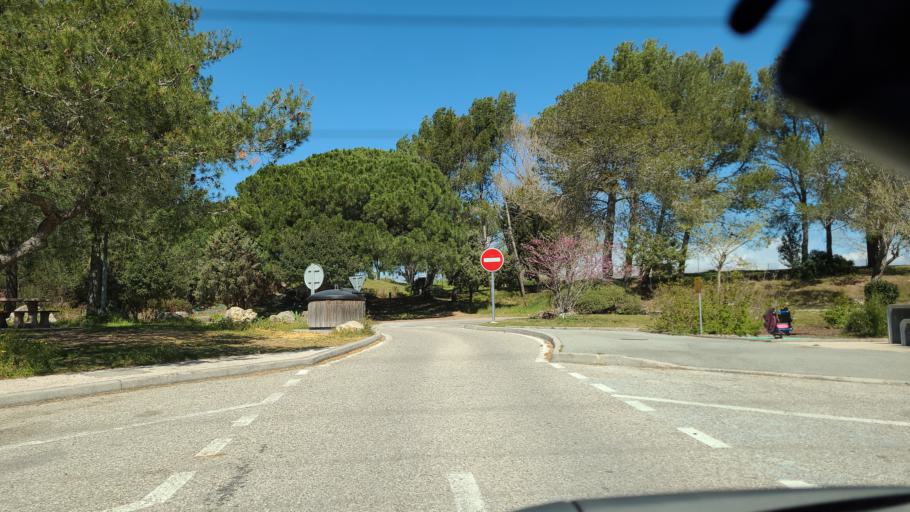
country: FR
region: Provence-Alpes-Cote d'Azur
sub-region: Departement du Var
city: Puget-sur-Argens
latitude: 43.4676
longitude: 6.6705
